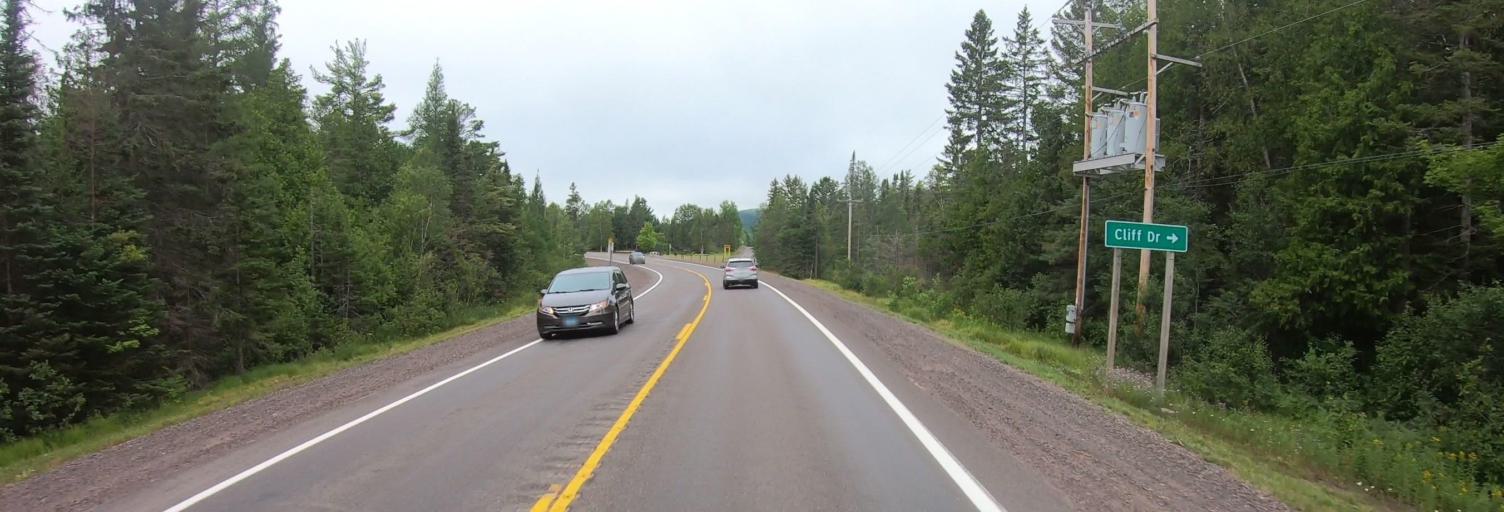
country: US
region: Michigan
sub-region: Keweenaw County
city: Eagle River
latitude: 47.3782
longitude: -88.3019
